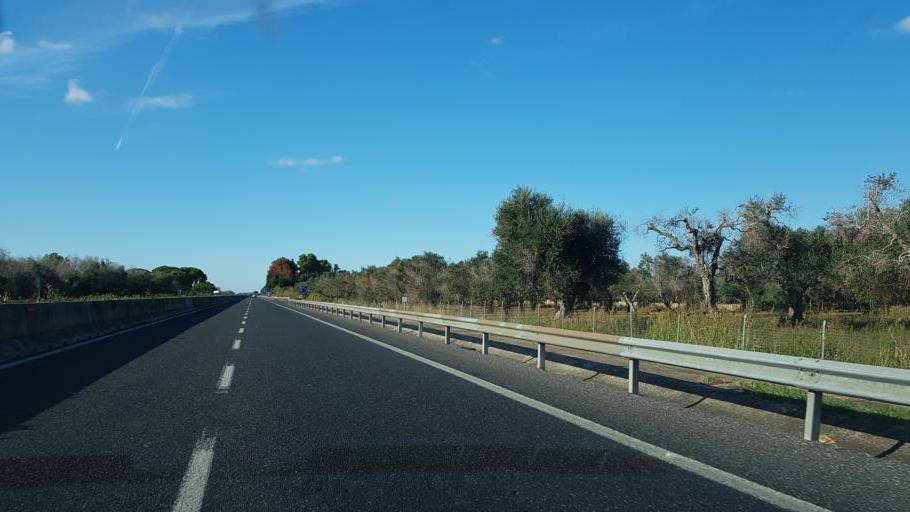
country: IT
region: Apulia
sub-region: Provincia di Brindisi
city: Torchiarolo
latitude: 40.4745
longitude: 18.0486
